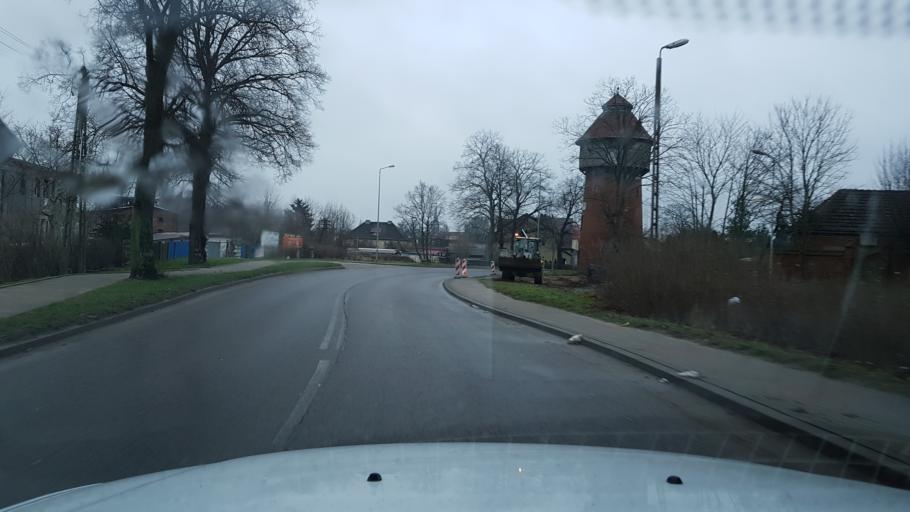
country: PL
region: West Pomeranian Voivodeship
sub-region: Powiat gryficki
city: Ploty
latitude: 53.8087
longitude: 15.2619
